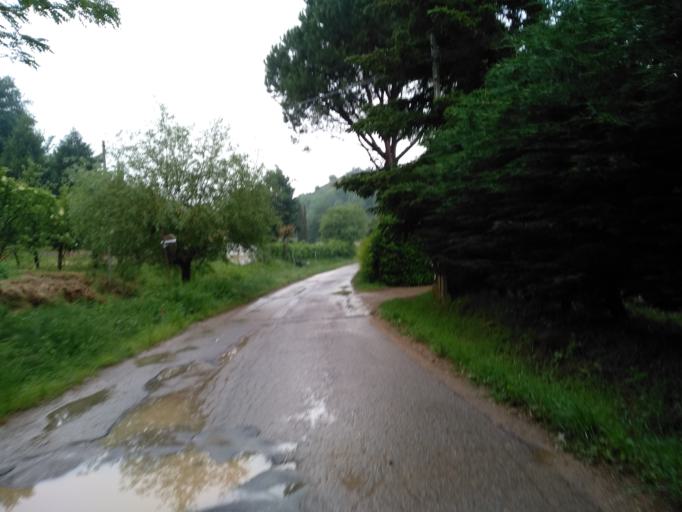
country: IT
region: Tuscany
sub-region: Province of Arezzo
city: San Giovanni Valdarno
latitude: 43.5564
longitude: 11.5176
